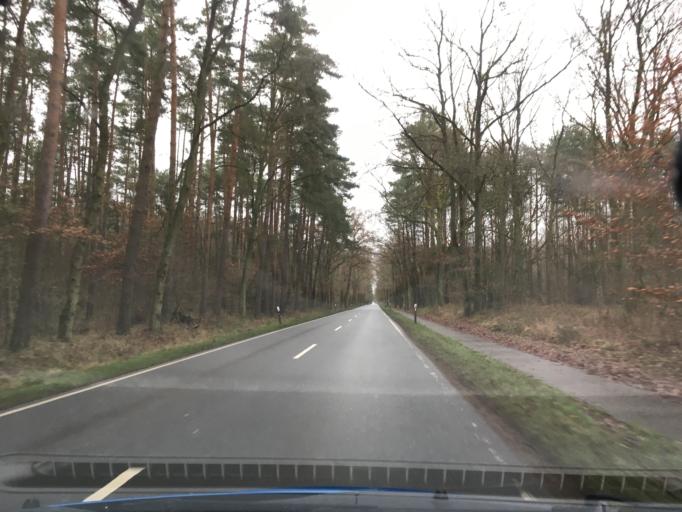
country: DE
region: Lower Saxony
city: Neetze
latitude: 53.2822
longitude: 10.6417
